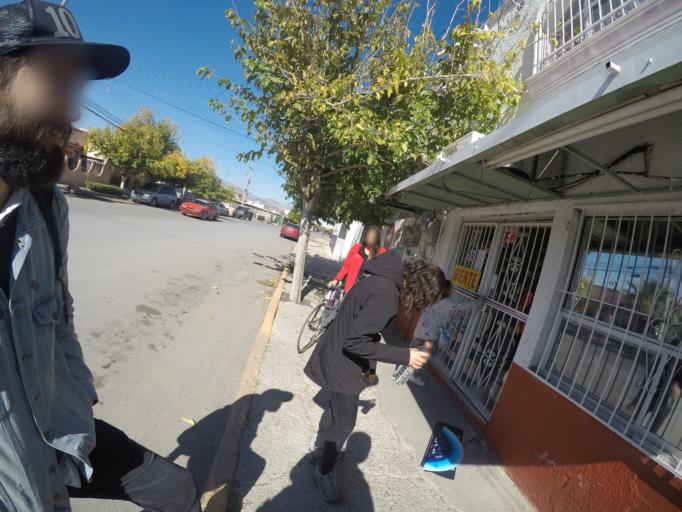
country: MX
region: Chihuahua
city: Ciudad Juarez
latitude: 31.7314
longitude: -106.4279
